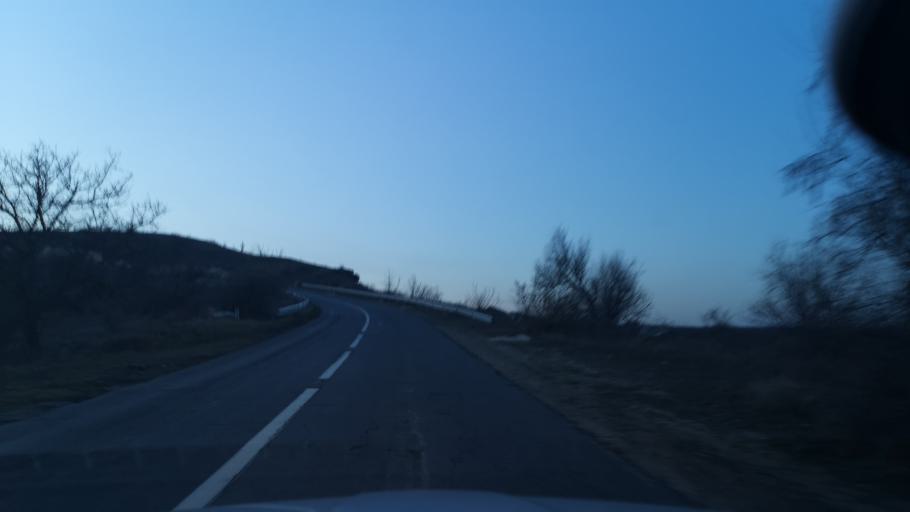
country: MD
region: Telenesti
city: Cocieri
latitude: 47.3102
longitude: 28.9715
